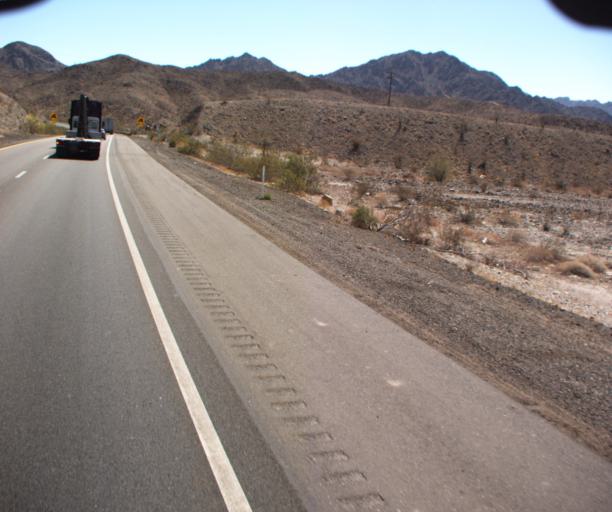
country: US
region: Arizona
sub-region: Yuma County
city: Fortuna Foothills
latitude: 32.6595
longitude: -114.3486
